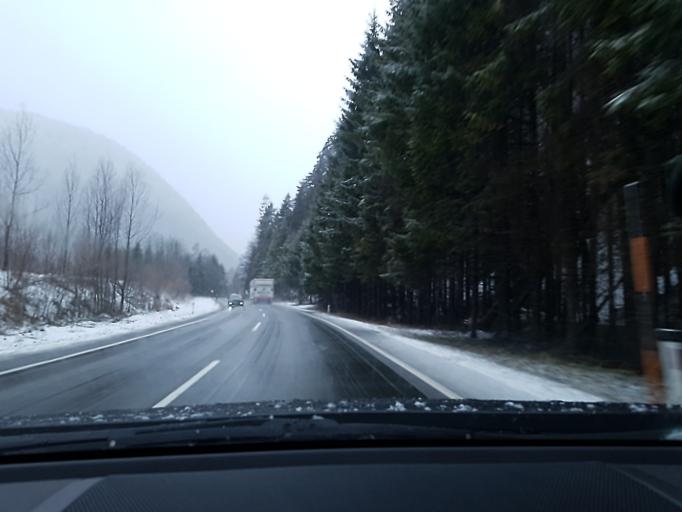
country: AT
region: Salzburg
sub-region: Politischer Bezirk Hallein
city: Scheffau am Tennengebirge
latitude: 47.5863
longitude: 13.2295
